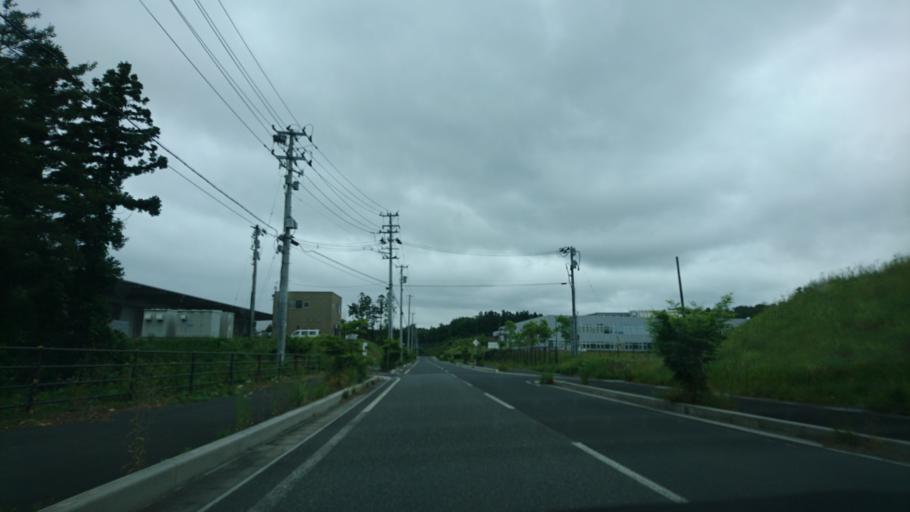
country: JP
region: Iwate
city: Ichinoseki
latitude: 38.9036
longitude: 141.1674
